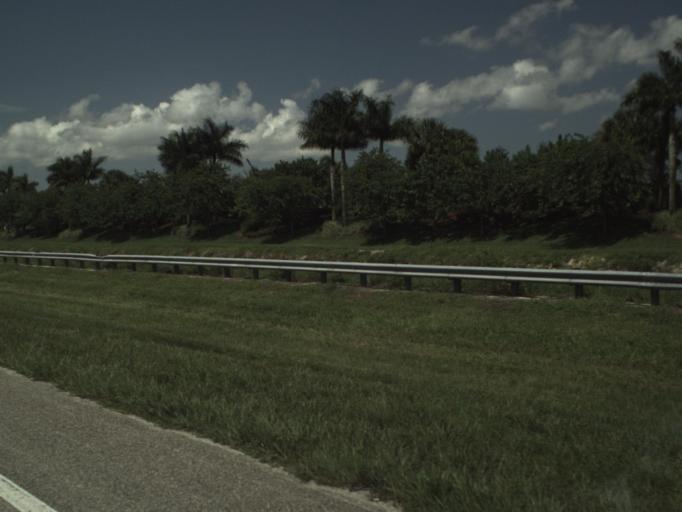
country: US
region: Florida
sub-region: Palm Beach County
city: Villages of Oriole
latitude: 26.5179
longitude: -80.2052
